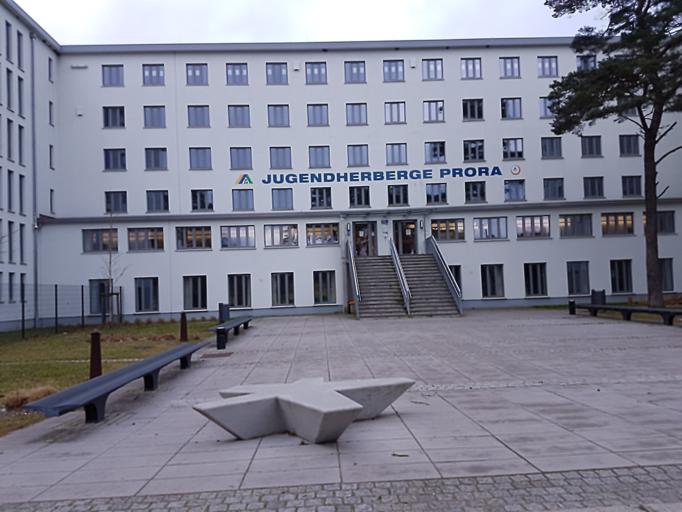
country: DE
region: Mecklenburg-Vorpommern
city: Ostseebad Binz
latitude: 54.4508
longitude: 13.5694
